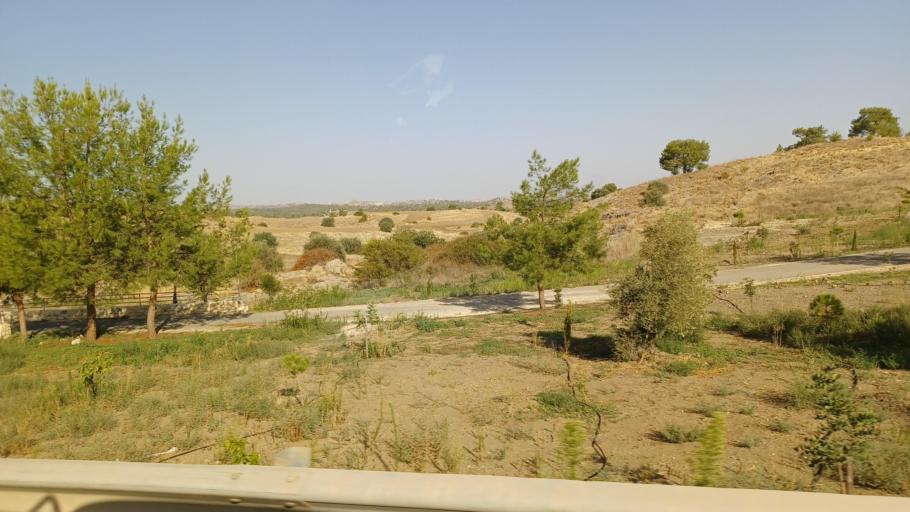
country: CY
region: Lefkosia
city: Lythrodontas
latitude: 34.9665
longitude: 33.3388
